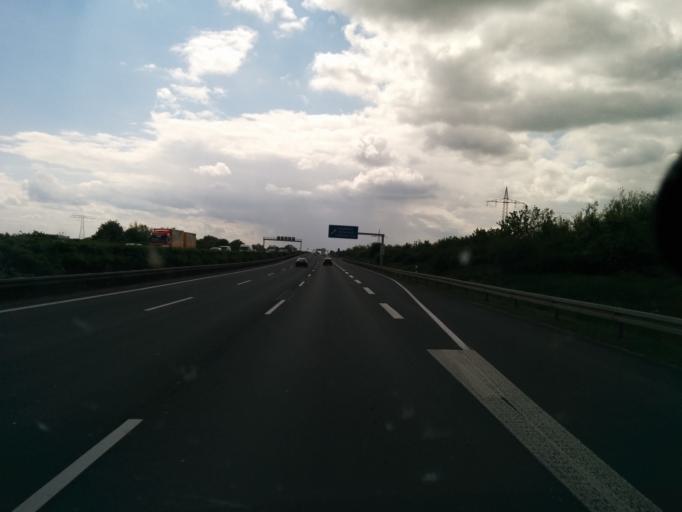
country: DE
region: Saxony-Anhalt
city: Glindenberg
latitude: 52.2153
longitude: 11.6717
